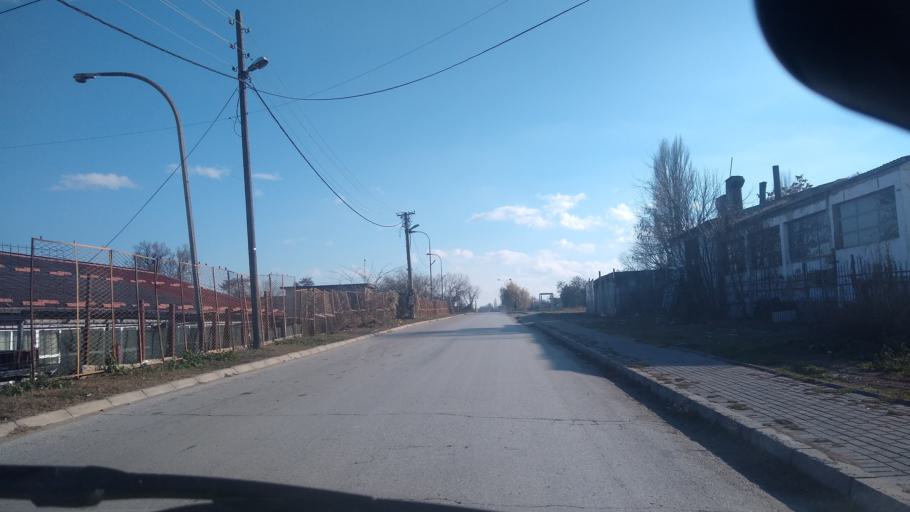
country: MK
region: Bitola
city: Bitola
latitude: 41.0133
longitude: 21.3459
